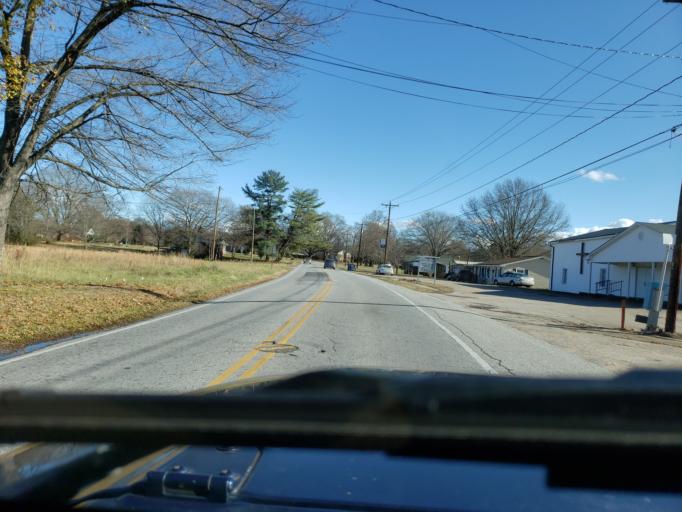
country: US
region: North Carolina
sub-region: Cleveland County
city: White Plains
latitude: 35.1772
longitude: -81.4550
